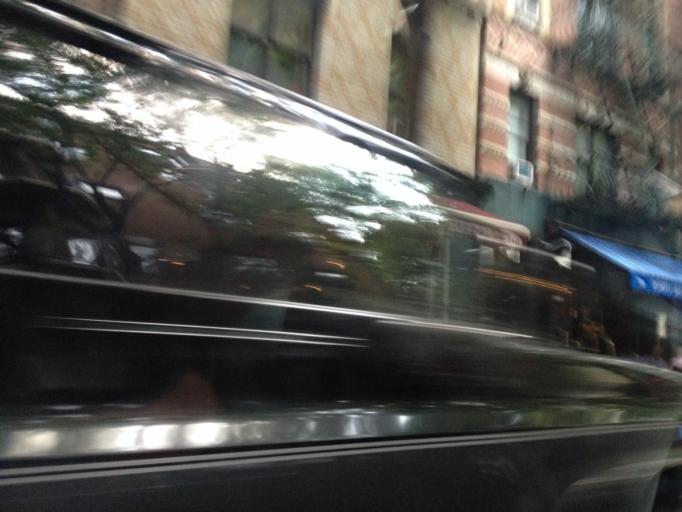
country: US
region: New York
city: New York City
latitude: 40.7288
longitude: -73.9993
